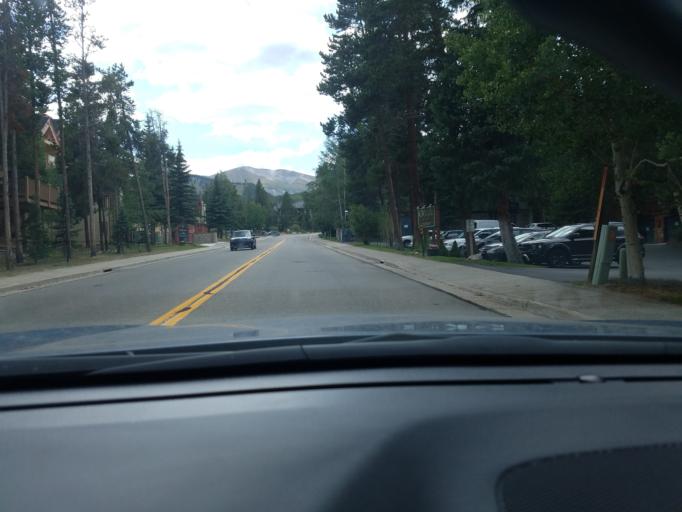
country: US
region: Colorado
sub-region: Summit County
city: Breckenridge
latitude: 39.4794
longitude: -106.0512
